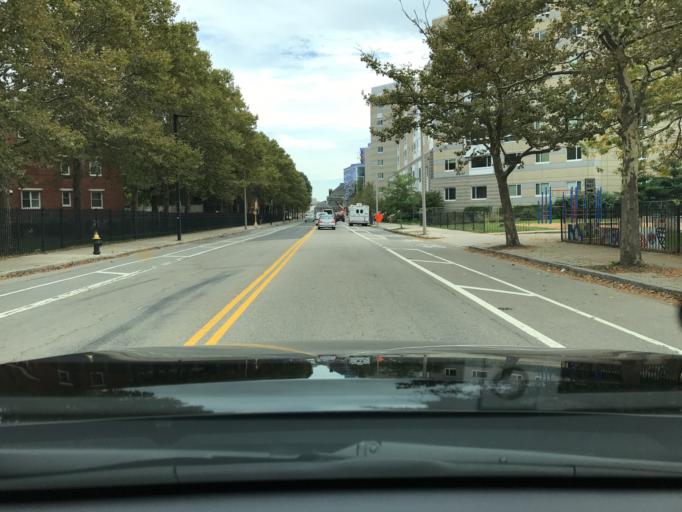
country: US
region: Massachusetts
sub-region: Suffolk County
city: South Boston
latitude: 42.3178
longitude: -71.0424
